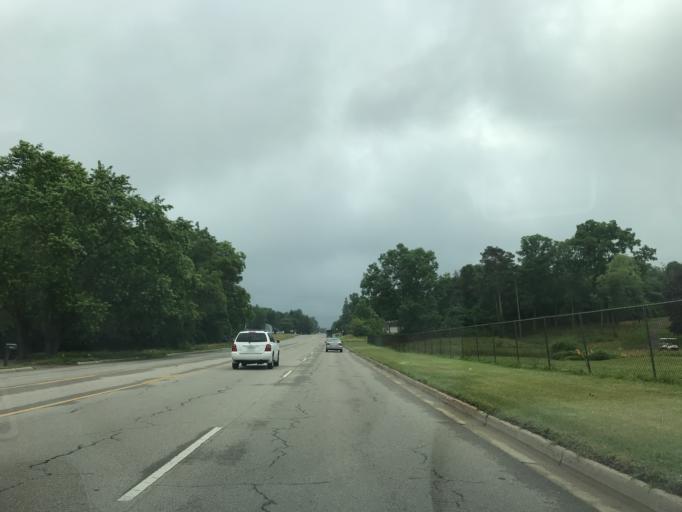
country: US
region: Michigan
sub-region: Washtenaw County
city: Ypsilanti
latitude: 42.2449
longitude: -83.6564
